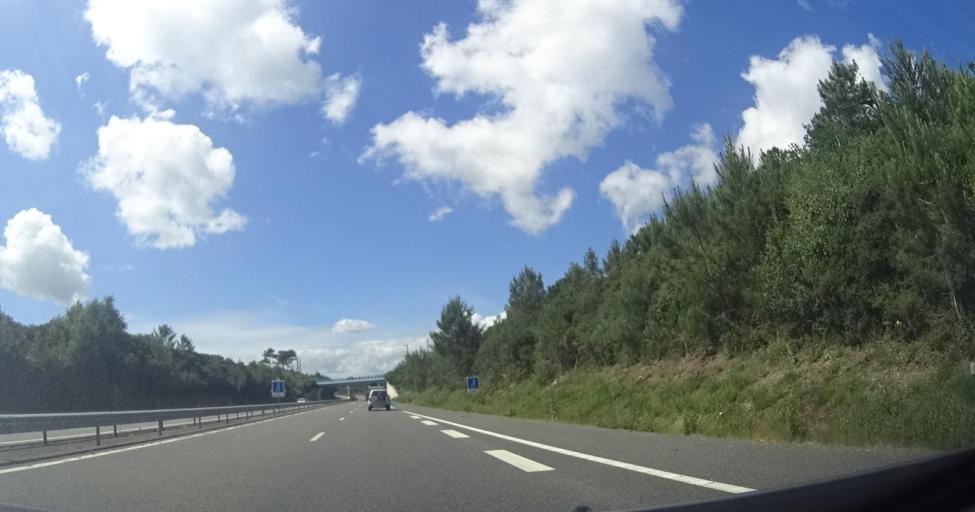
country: FR
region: Brittany
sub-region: Departement du Morbihan
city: Pluherlin
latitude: 47.6719
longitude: -2.3615
